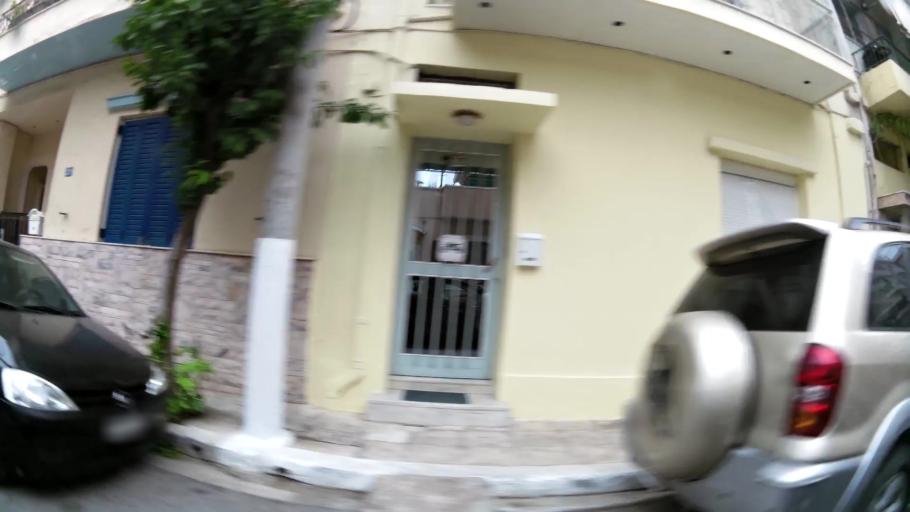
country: GR
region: Attica
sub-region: Nomos Piraios
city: Agios Ioannis Rentis
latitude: 37.9544
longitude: 23.6624
